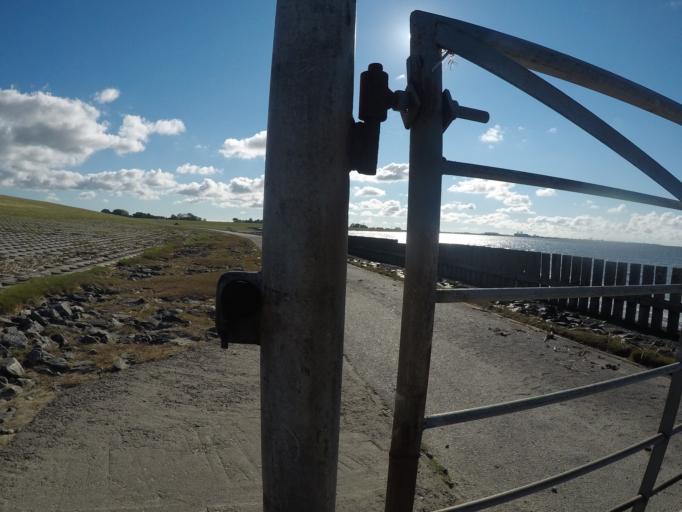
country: DE
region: Lower Saxony
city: Nordleda
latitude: 53.8323
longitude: 8.8307
